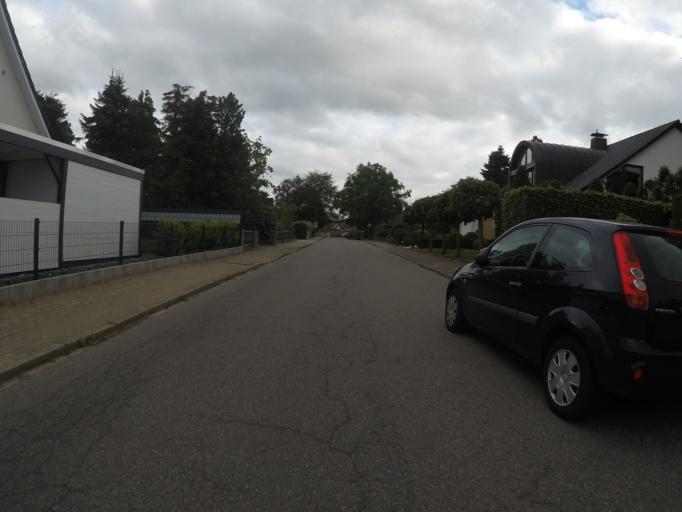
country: DE
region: Schleswig-Holstein
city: Quickborn
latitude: 53.7271
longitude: 9.9108
